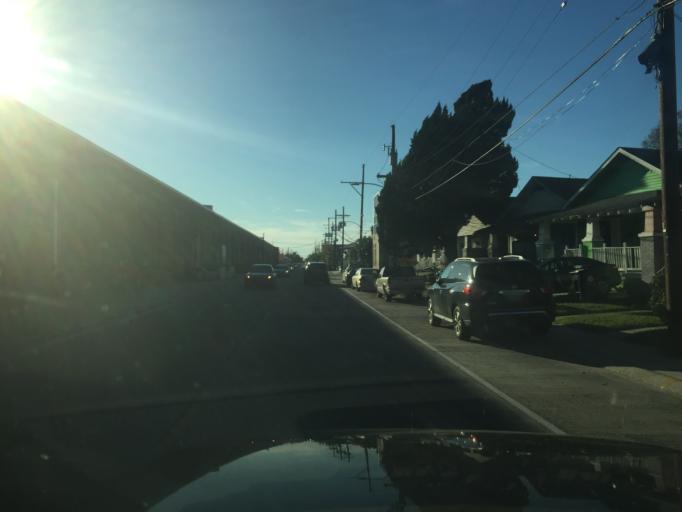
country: US
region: Louisiana
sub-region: Jefferson Parish
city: Harvey
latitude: 29.9180
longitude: -90.0914
